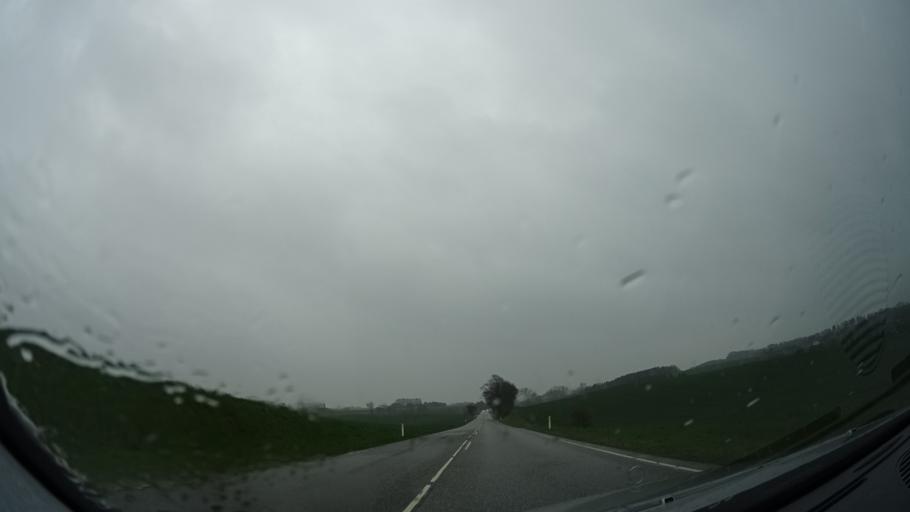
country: DK
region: Zealand
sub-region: Odsherred Kommune
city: Asnaes
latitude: 55.8209
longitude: 11.5770
